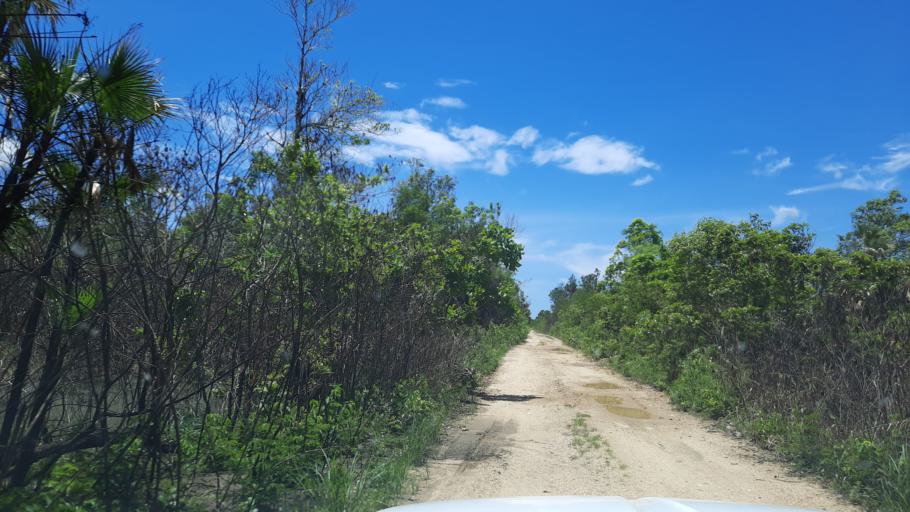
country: BZ
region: Cayo
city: Belmopan
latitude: 17.3775
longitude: -88.4888
